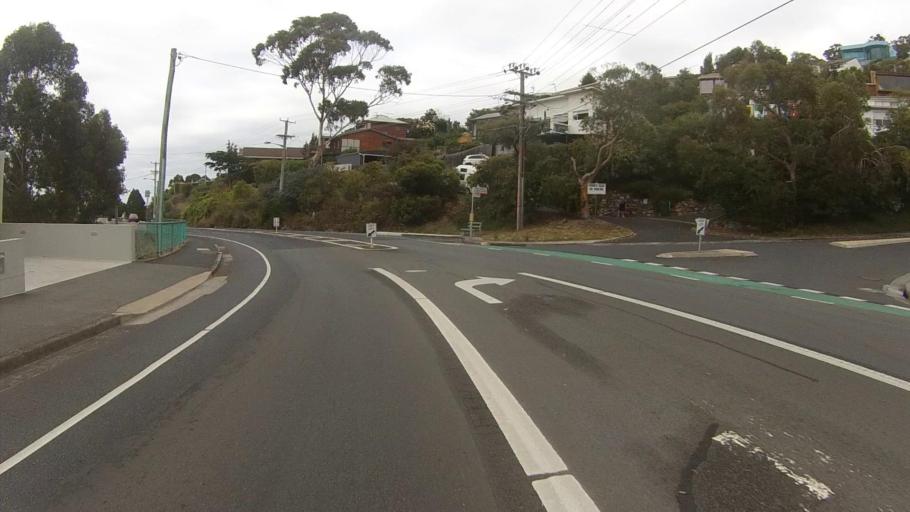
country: AU
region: Tasmania
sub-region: Kingborough
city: Taroona
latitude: -42.9243
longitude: 147.3602
